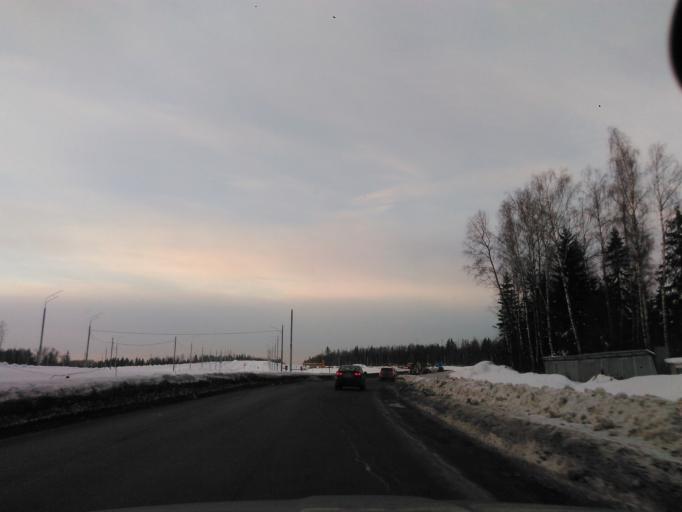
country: RU
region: Moskovskaya
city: Povarovo
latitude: 56.0106
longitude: 37.0275
